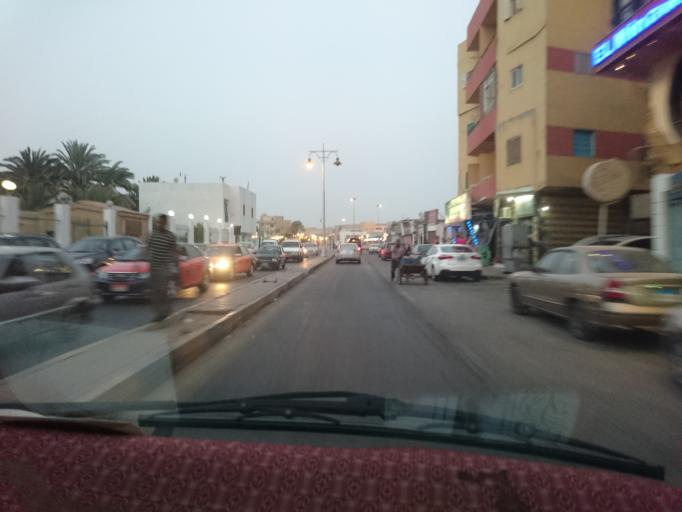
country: EG
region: Red Sea
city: Hurghada
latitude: 27.2298
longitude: 33.8414
